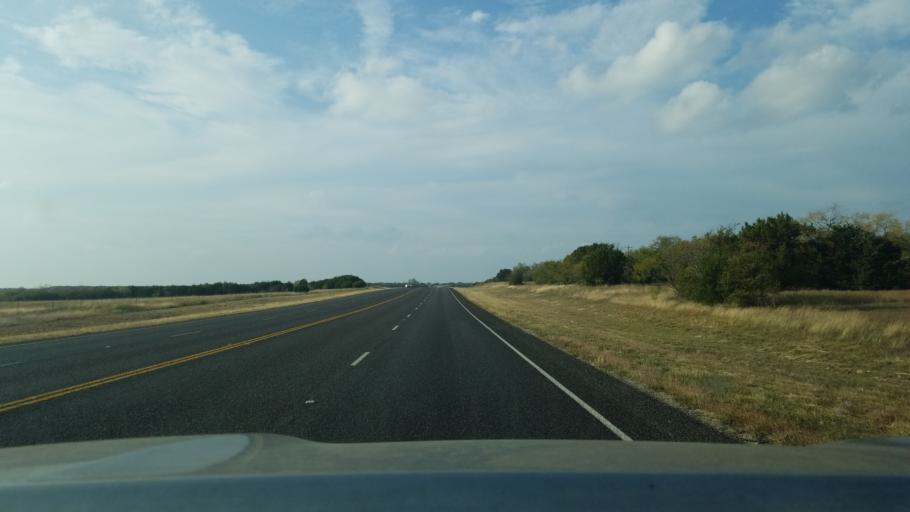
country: US
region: Texas
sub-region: Mills County
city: Goldthwaite
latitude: 31.2313
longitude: -98.4114
